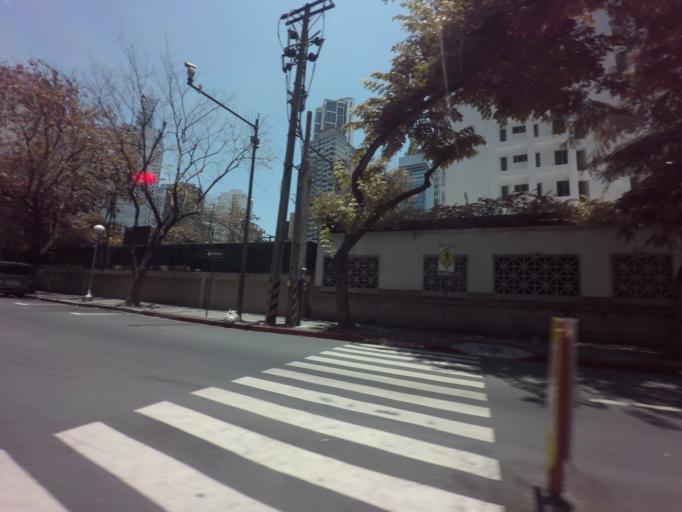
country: PH
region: Metro Manila
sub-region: Makati City
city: Makati City
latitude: 14.5596
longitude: 121.0221
